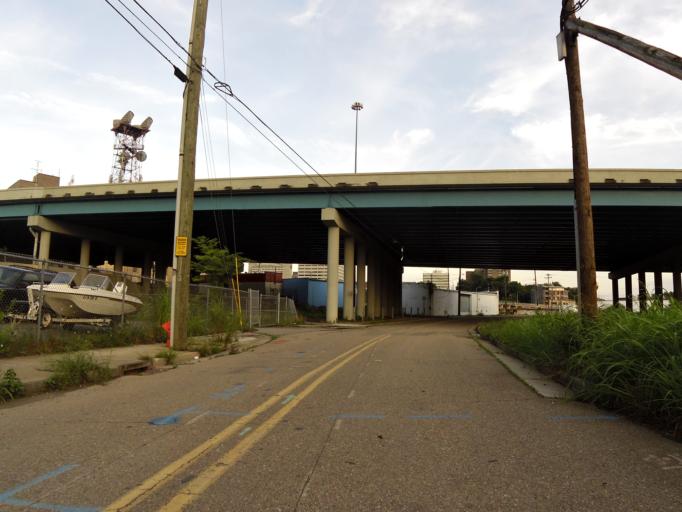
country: US
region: Tennessee
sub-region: Knox County
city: Knoxville
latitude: 35.9705
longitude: -83.9253
